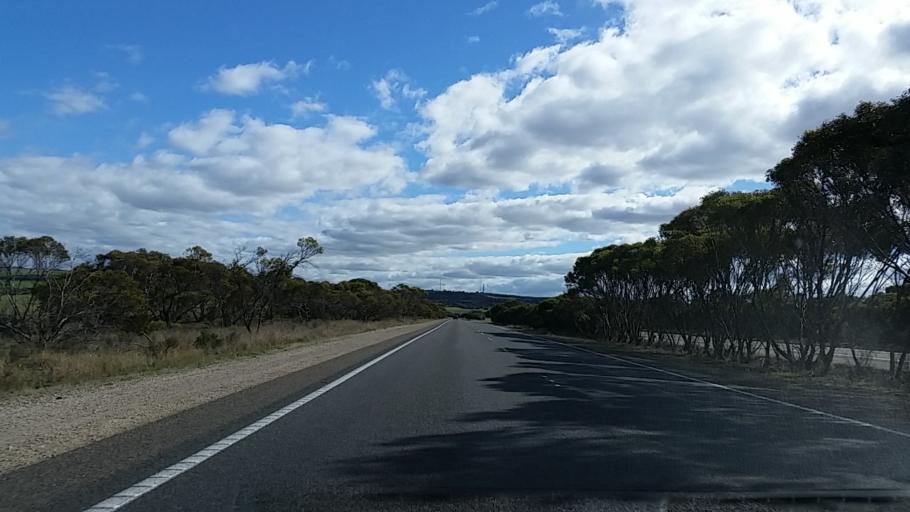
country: AU
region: South Australia
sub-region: Murray Bridge
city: Murray Bridge
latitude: -35.1467
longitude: 139.2573
